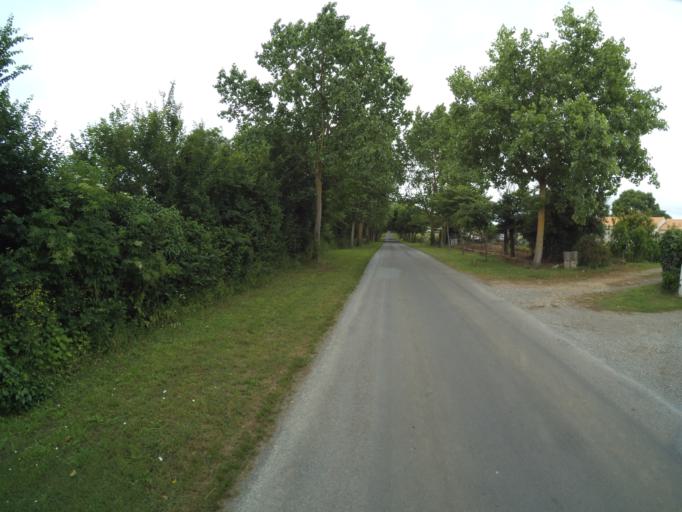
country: FR
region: Poitou-Charentes
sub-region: Departement de la Charente-Maritime
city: Saint-Laurent-de-la-Pree
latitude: 45.9877
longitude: -1.0141
